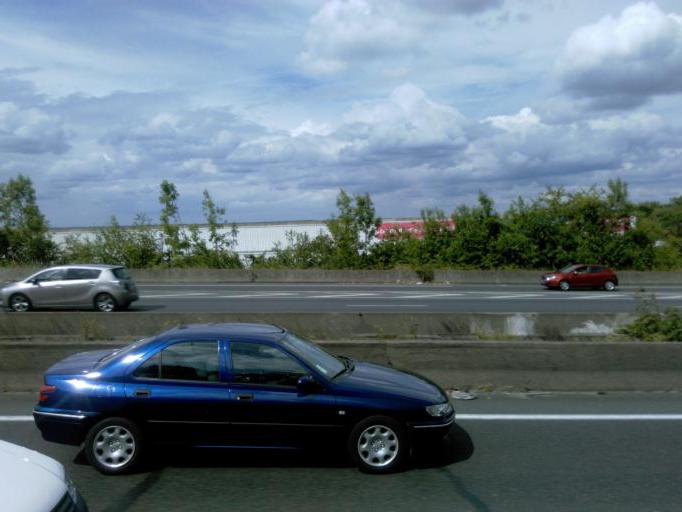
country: FR
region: Ile-de-France
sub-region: Departement du Val-d'Oise
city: Franconville
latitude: 48.9766
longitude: 2.2351
